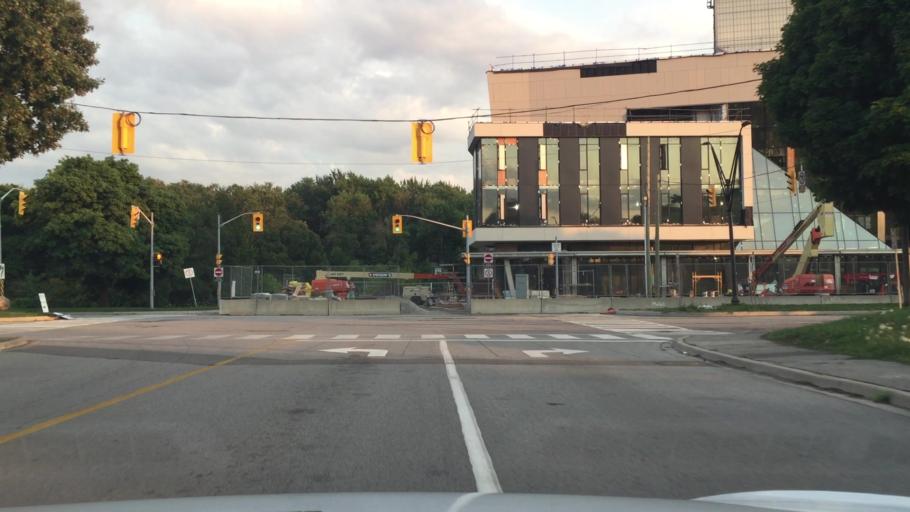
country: CA
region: Ontario
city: Concord
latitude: 43.7749
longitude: -79.4970
